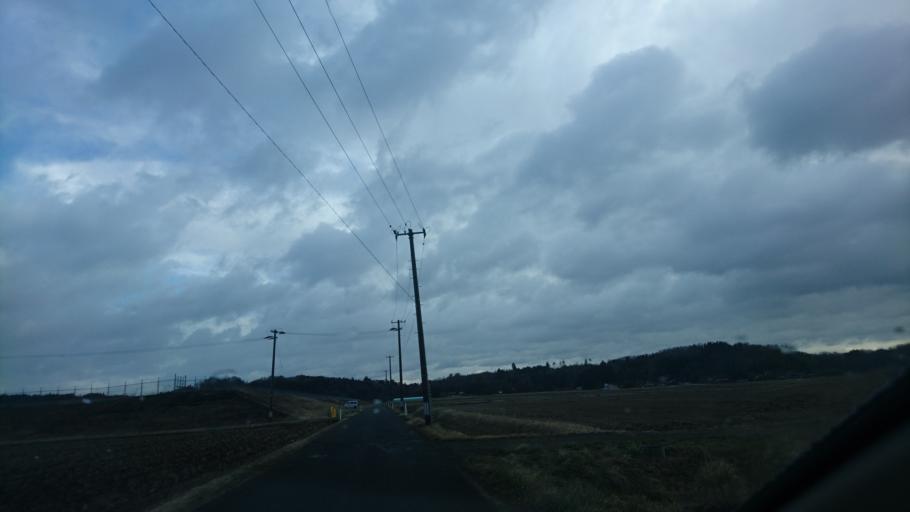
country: JP
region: Iwate
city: Ichinoseki
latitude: 38.7791
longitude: 141.0312
